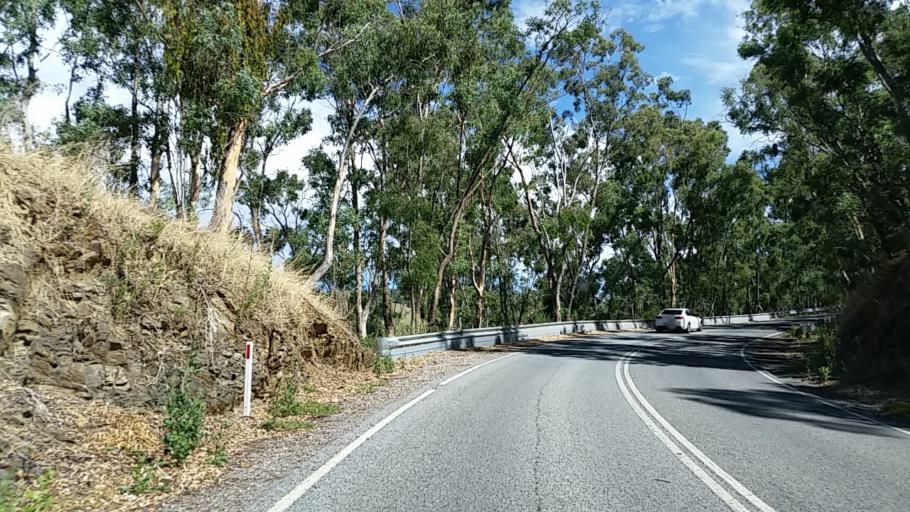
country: AU
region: South Australia
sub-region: Tea Tree Gully
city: Golden Grove
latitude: -34.8524
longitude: 138.7915
